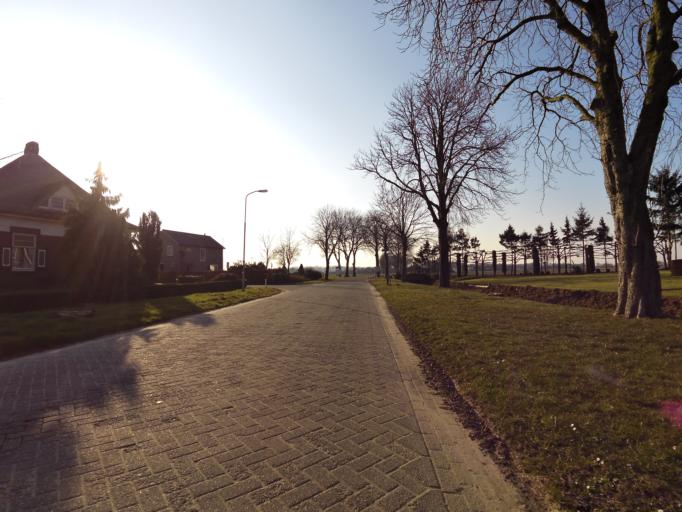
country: NL
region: Gelderland
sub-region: Gemeente Montferland
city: s-Heerenberg
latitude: 51.8890
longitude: 6.3007
